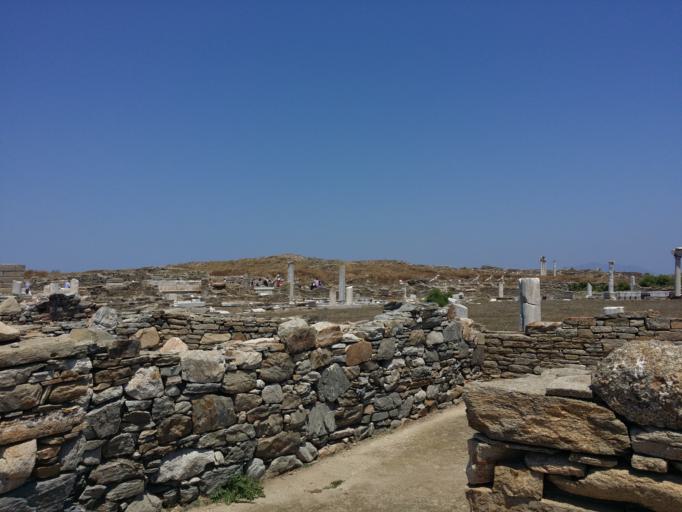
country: GR
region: South Aegean
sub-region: Nomos Kykladon
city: Mykonos
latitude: 37.4014
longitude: 25.2675
